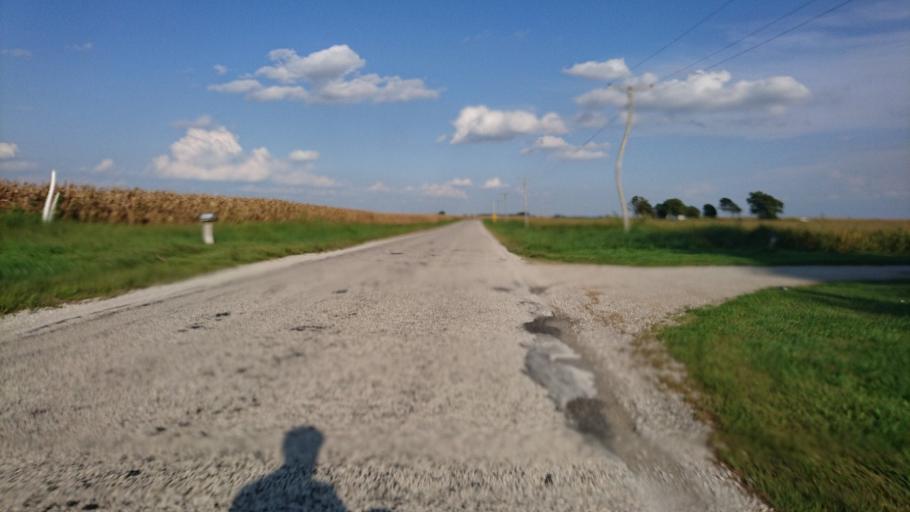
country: US
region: Illinois
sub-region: Logan County
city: Atlanta
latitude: 40.2598
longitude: -89.2102
